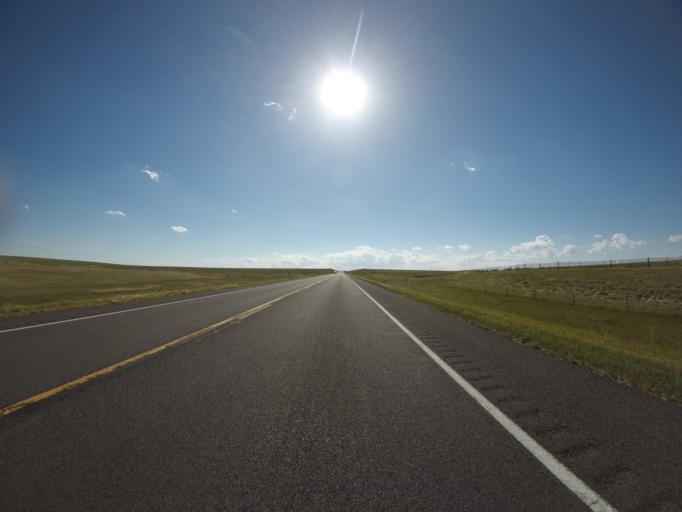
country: US
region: Colorado
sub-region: Logan County
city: Sterling
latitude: 40.6110
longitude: -103.5600
